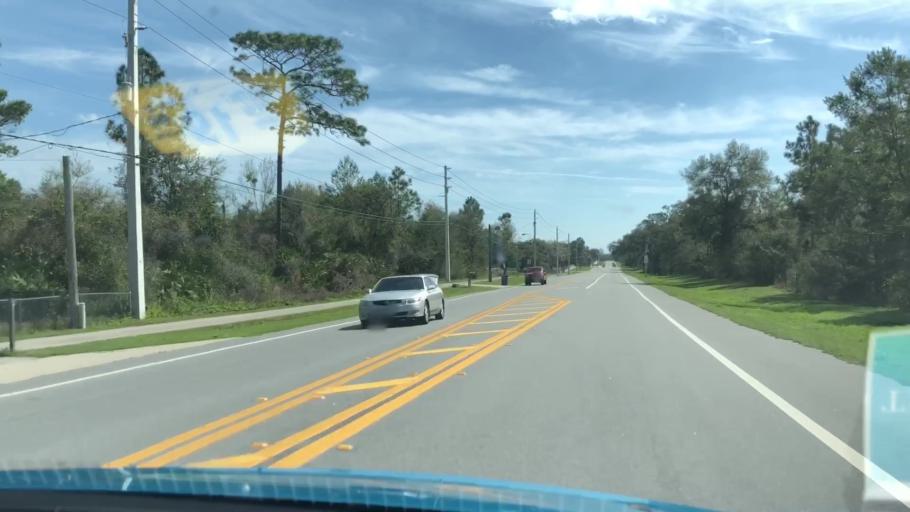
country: US
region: Florida
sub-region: Seminole County
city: Midway
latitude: 28.8544
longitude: -81.1797
